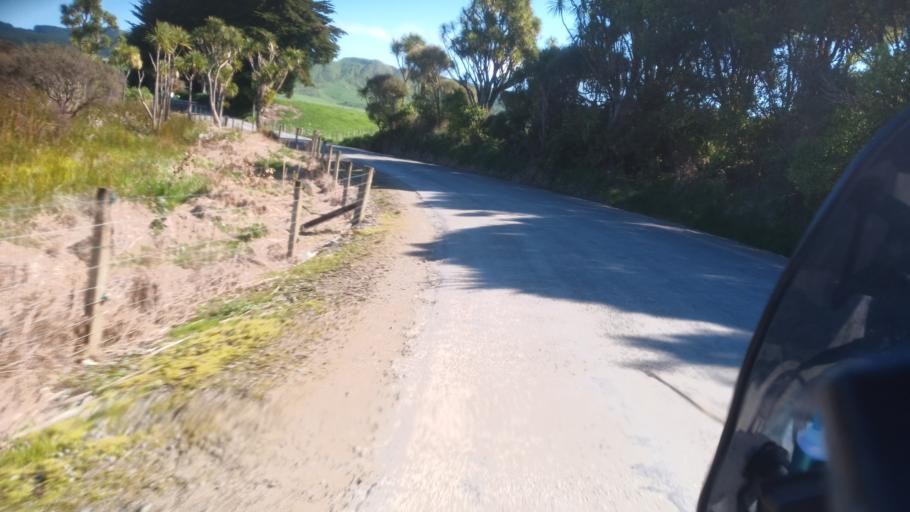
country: NZ
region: Gisborne
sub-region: Gisborne District
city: Gisborne
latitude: -39.1420
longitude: 177.9253
